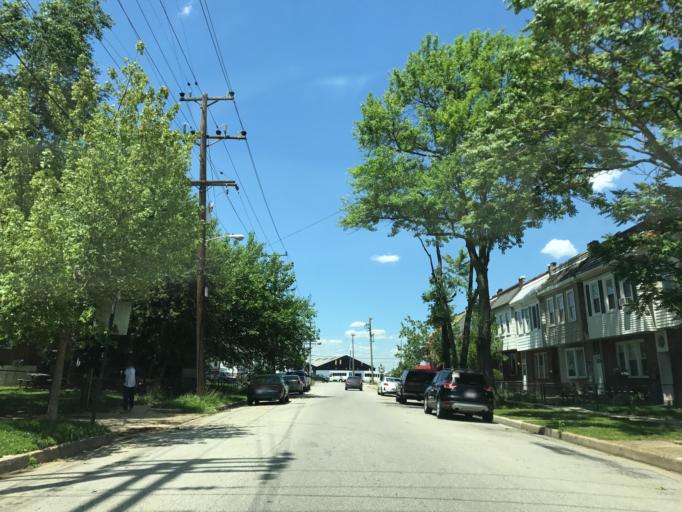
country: US
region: Maryland
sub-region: Anne Arundel County
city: Brooklyn Park
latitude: 39.2313
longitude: -76.5905
